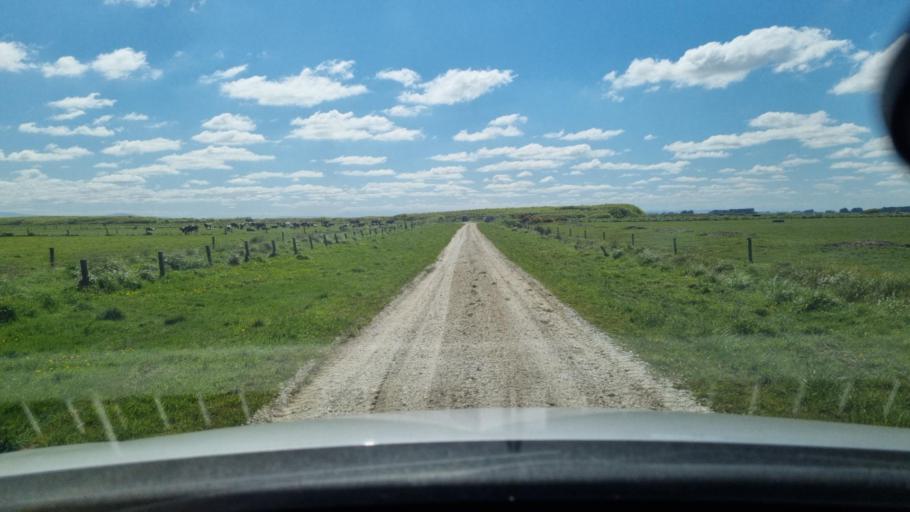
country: NZ
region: Southland
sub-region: Invercargill City
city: Invercargill
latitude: -46.3861
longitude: 168.2575
